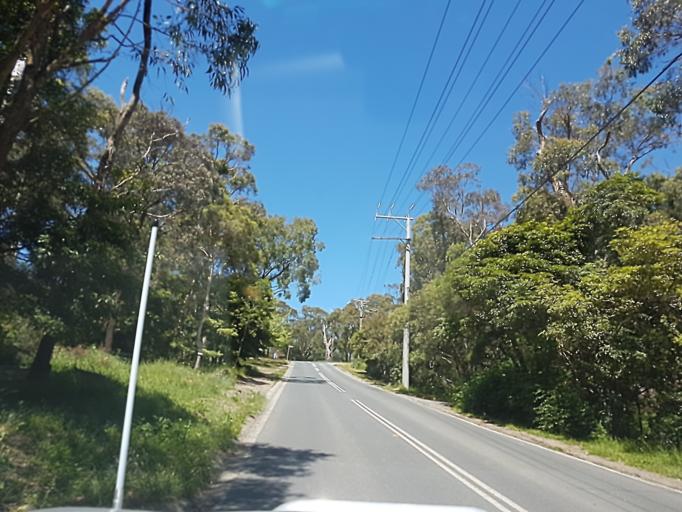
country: AU
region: Victoria
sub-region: Yarra Ranges
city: Selby
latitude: -37.9190
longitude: 145.3690
